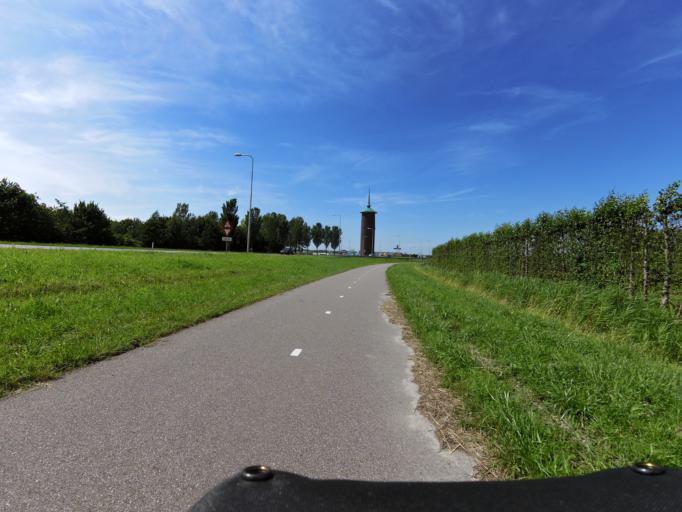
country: NL
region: South Holland
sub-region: Gemeente Goeree-Overflakkee
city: Dirksland
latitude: 51.7491
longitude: 4.1244
